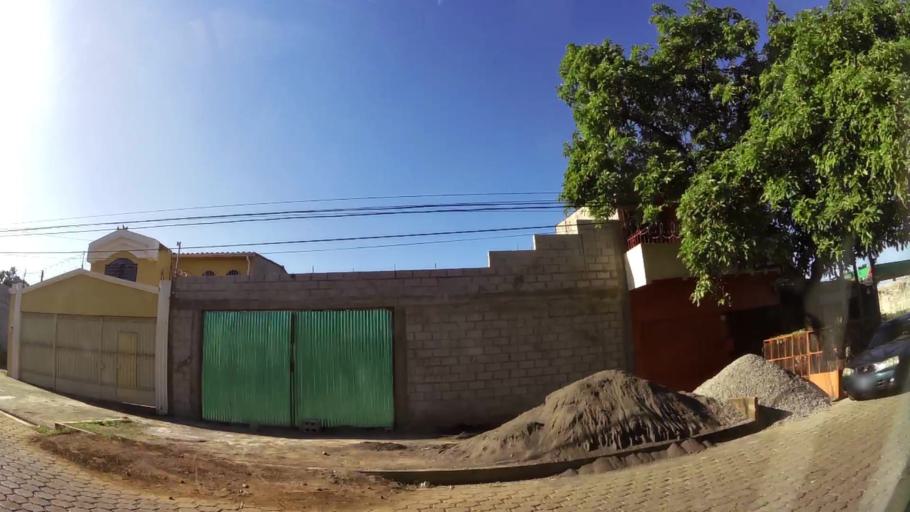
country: SV
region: Sonsonate
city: Sonzacate
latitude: 13.7326
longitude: -89.7122
